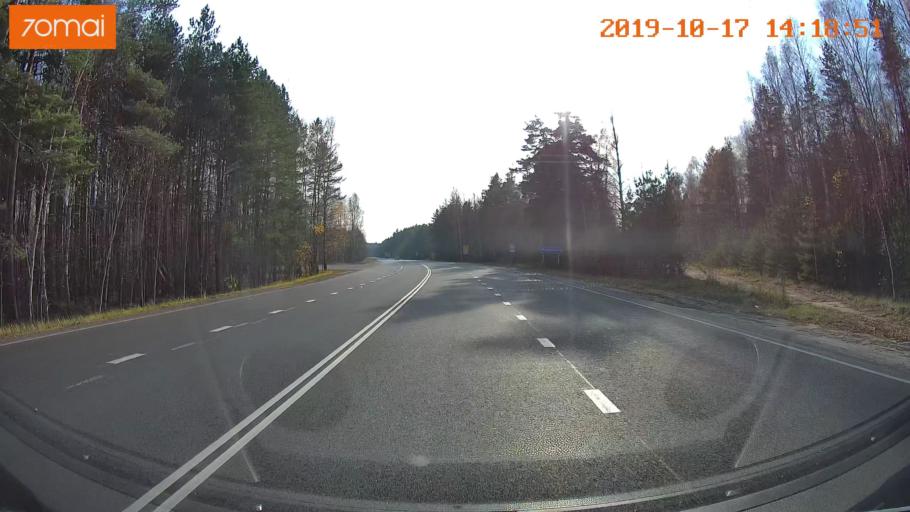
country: RU
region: Rjazan
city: Spas-Klepiki
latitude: 55.0579
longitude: 40.0258
